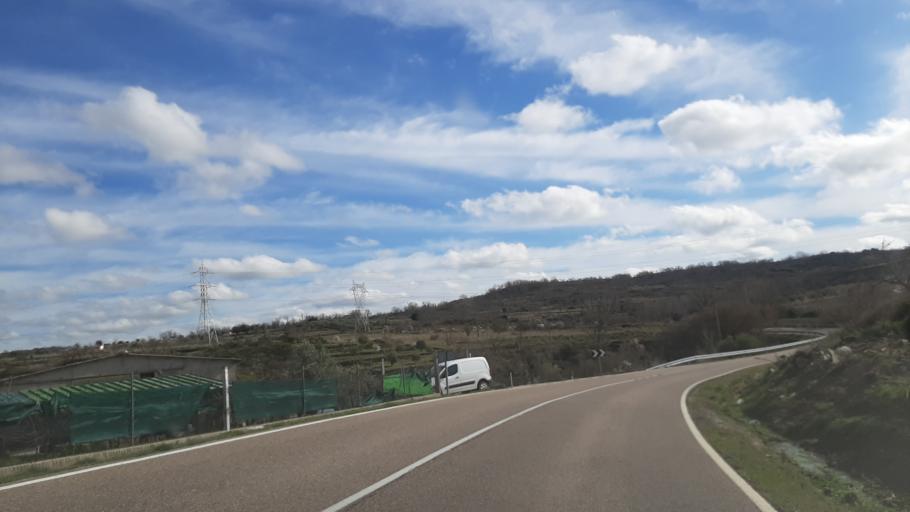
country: ES
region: Castille and Leon
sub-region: Provincia de Salamanca
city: Villarino de los Aires
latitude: 41.2656
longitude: -6.4513
